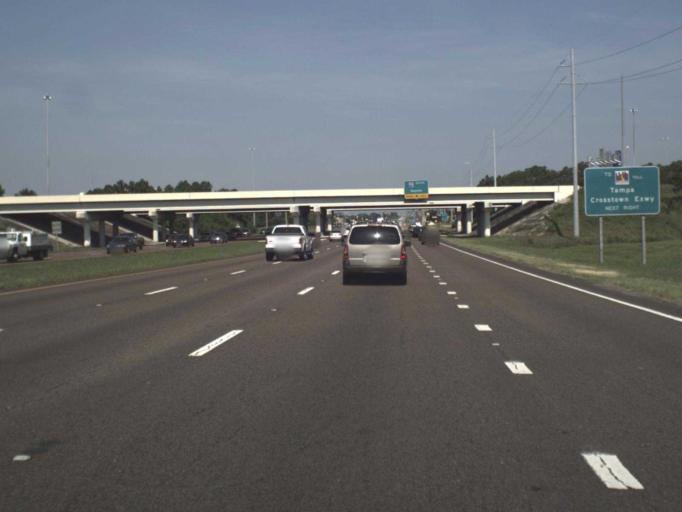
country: US
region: Florida
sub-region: Hillsborough County
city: Brandon
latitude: 27.9411
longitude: -82.3276
